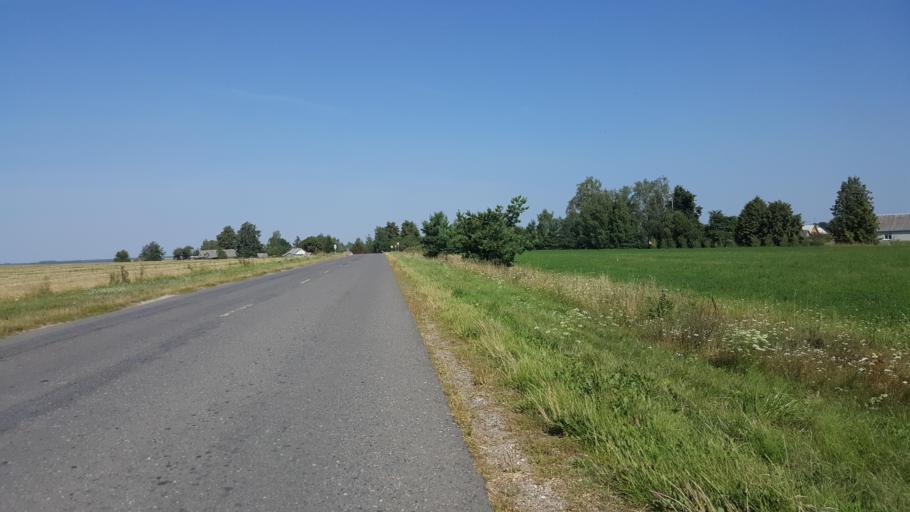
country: BY
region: Brest
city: Kamyanyets
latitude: 52.4639
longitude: 23.7179
